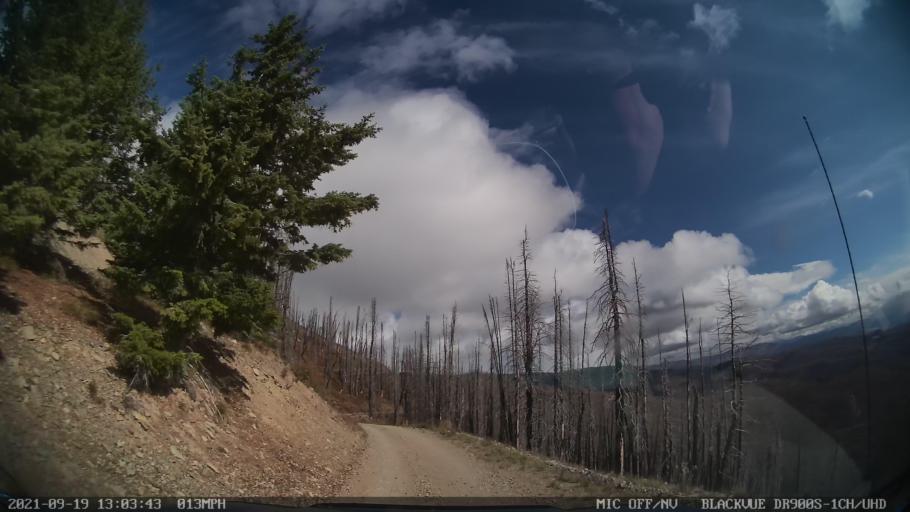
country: US
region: Montana
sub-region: Missoula County
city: Seeley Lake
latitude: 47.1836
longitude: -113.3555
